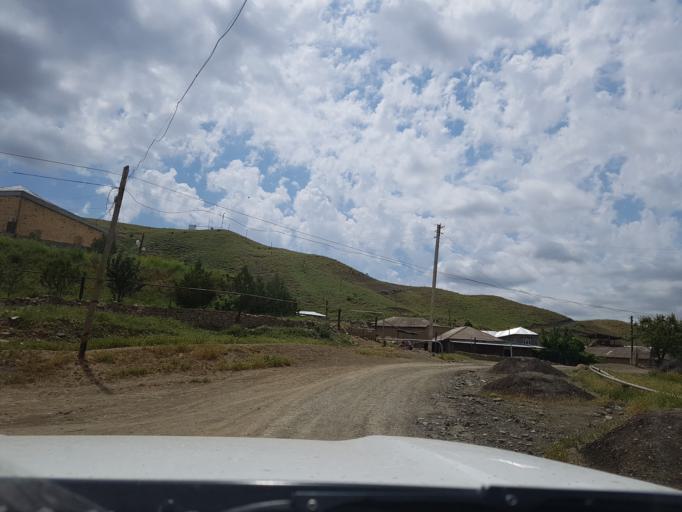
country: TM
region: Ahal
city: Baharly
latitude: 38.2008
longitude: 57.0053
